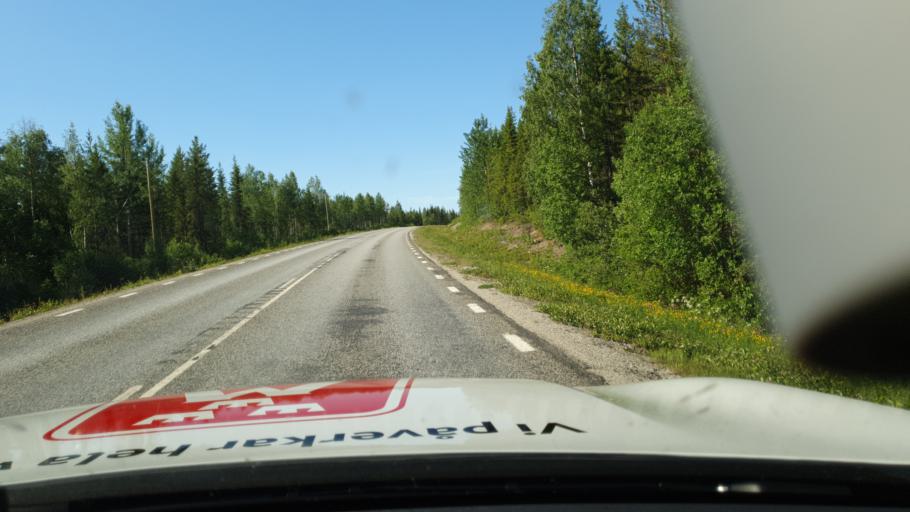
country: SE
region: Vaesterbotten
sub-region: Lycksele Kommun
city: Lycksele
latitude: 64.5443
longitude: 18.5044
